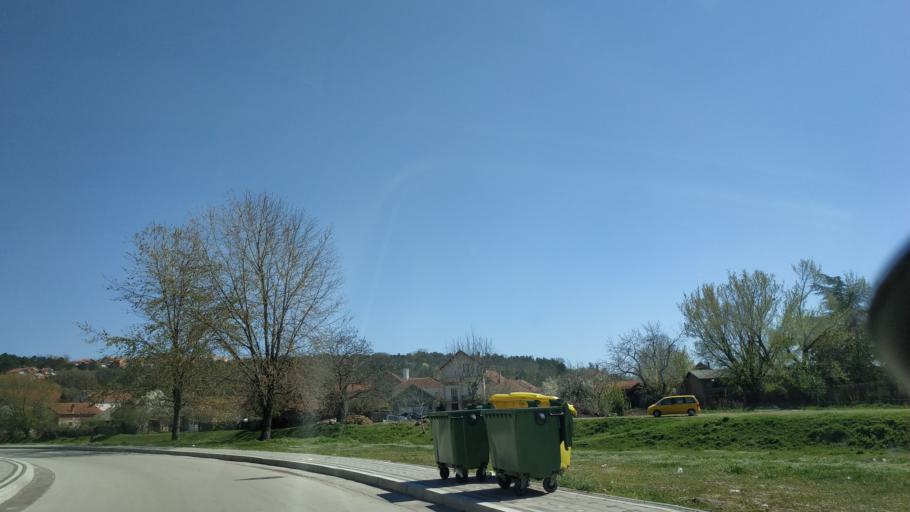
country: RS
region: Central Serbia
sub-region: Nisavski Okrug
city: Aleksinac
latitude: 43.5364
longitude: 21.7067
